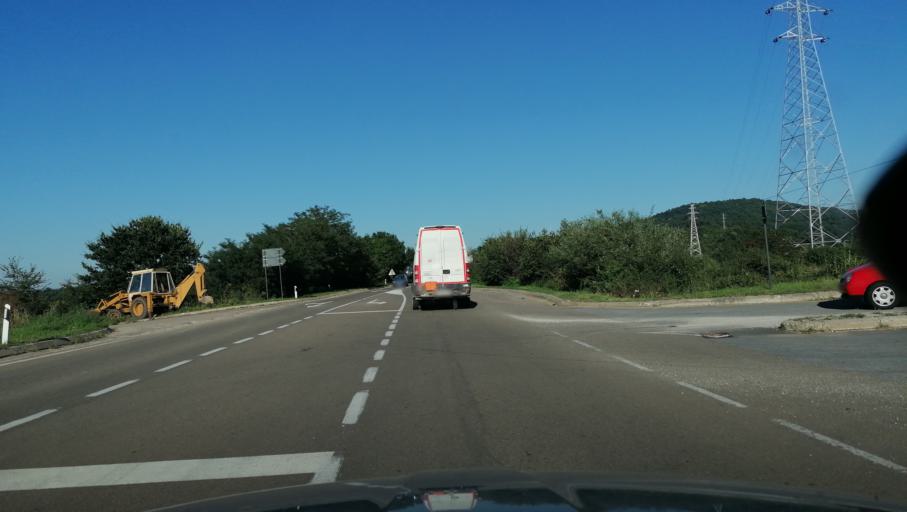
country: RS
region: Central Serbia
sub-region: Sumadijski Okrug
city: Knic
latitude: 43.9221
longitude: 20.6729
